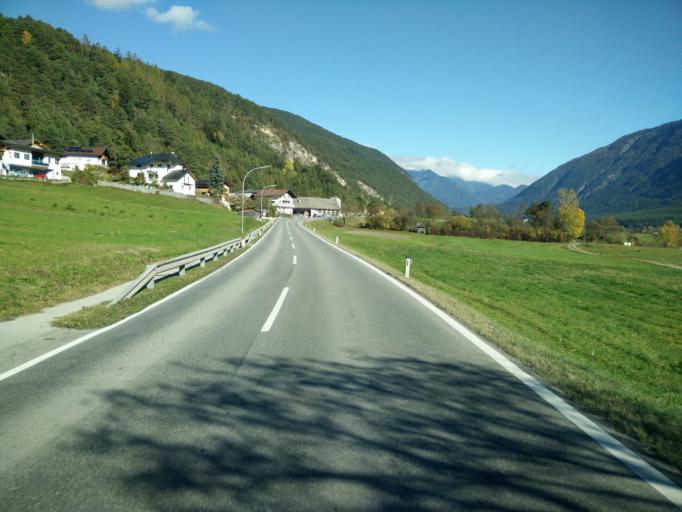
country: AT
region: Tyrol
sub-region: Politischer Bezirk Imst
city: Tarrenz
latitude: 47.2696
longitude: 10.7765
